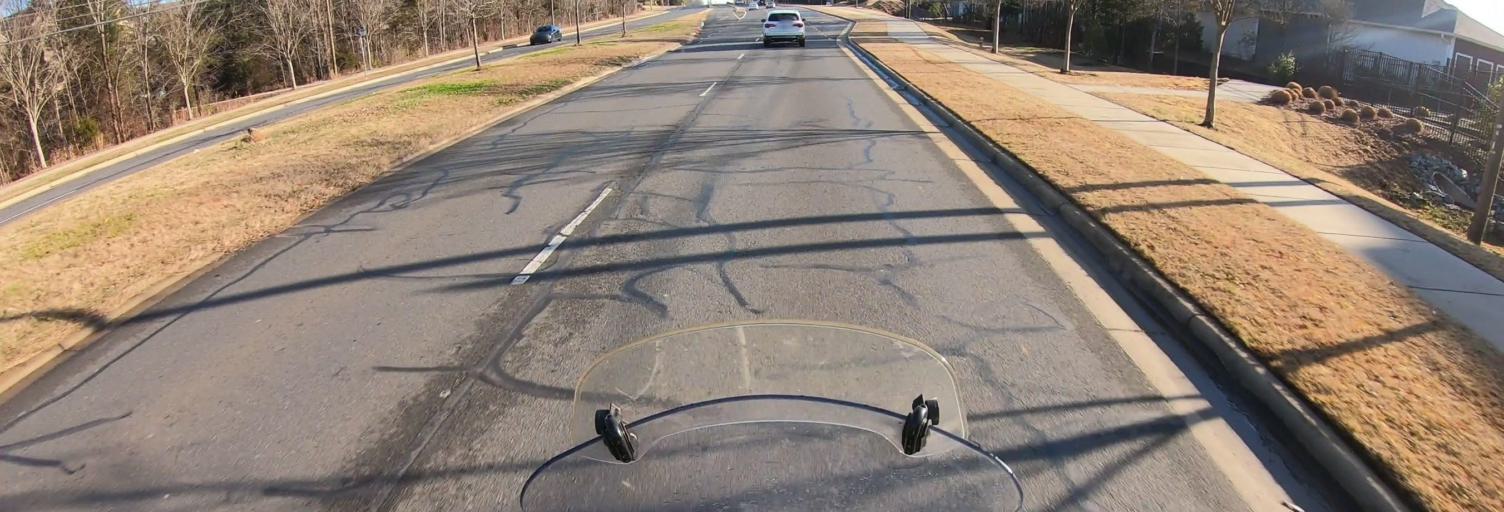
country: US
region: South Carolina
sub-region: York County
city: Lake Wylie
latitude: 35.1059
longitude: -80.9825
